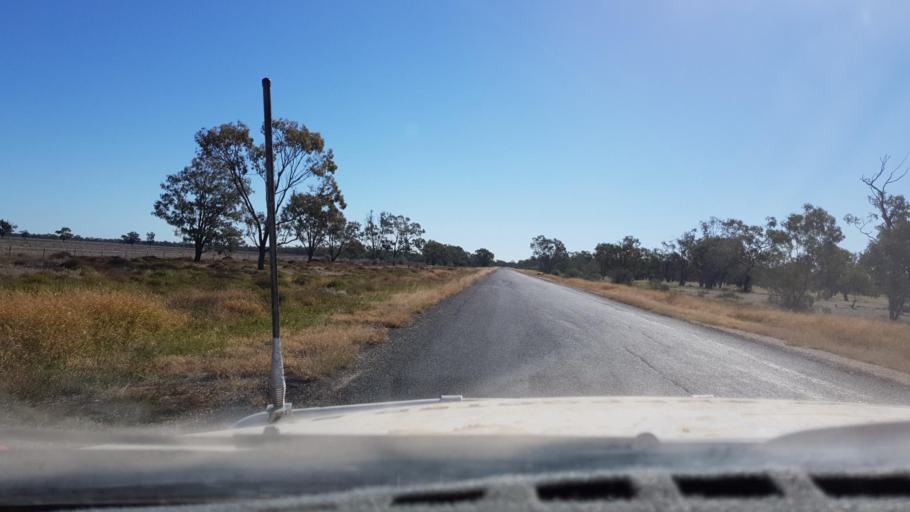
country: AU
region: New South Wales
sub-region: Walgett
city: Lightning Ridge
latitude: -29.5748
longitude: 148.6738
